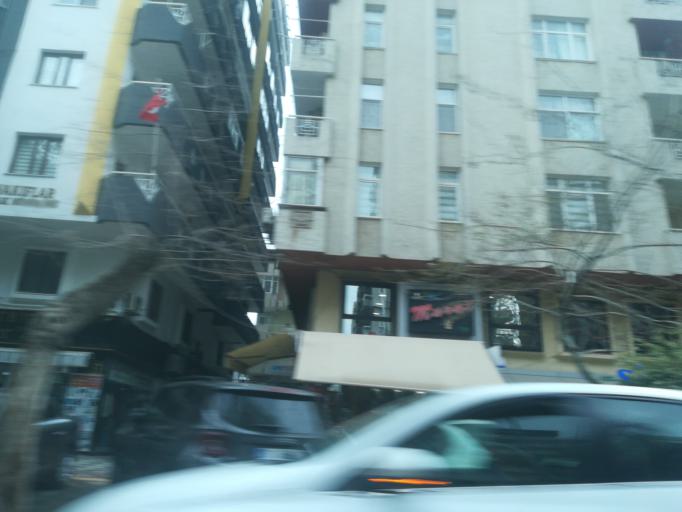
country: TR
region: Adana
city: Adana
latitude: 36.9947
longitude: 35.3225
